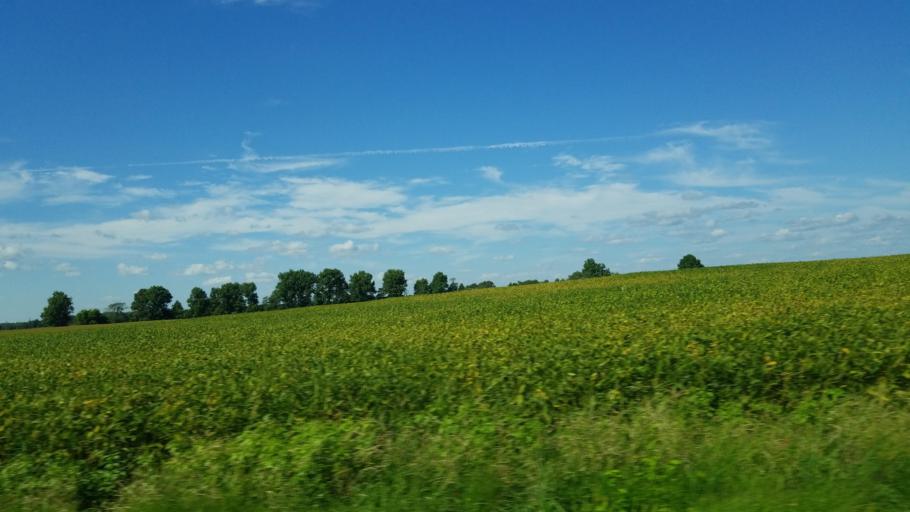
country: US
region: Illinois
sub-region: Williamson County
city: Johnston City
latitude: 37.7905
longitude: -88.7736
